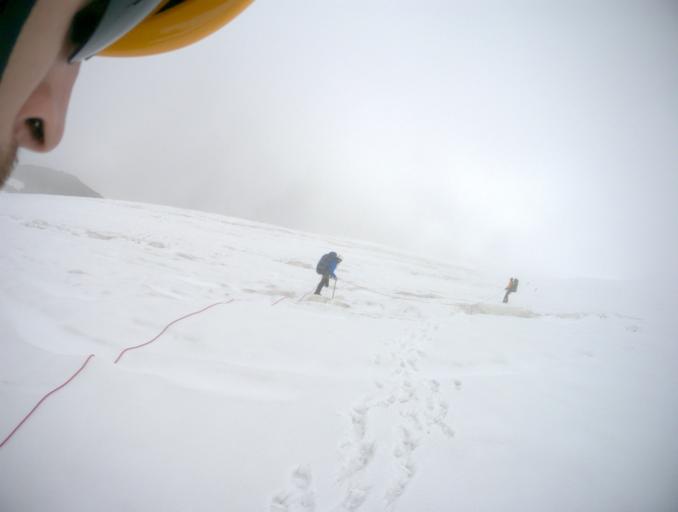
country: RU
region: Kabardino-Balkariya
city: Terskol
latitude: 43.3804
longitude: 42.4598
